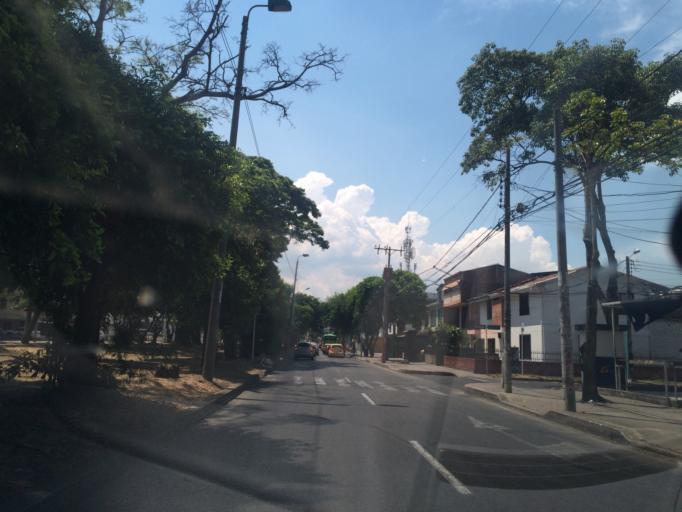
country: CO
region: Valle del Cauca
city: Cali
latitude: 3.4703
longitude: -76.5025
